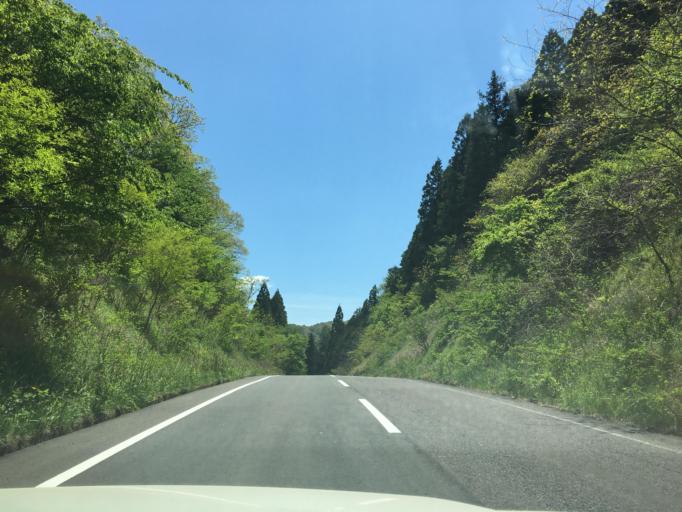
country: JP
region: Fukushima
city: Funehikimachi-funehiki
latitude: 37.3634
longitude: 140.6348
